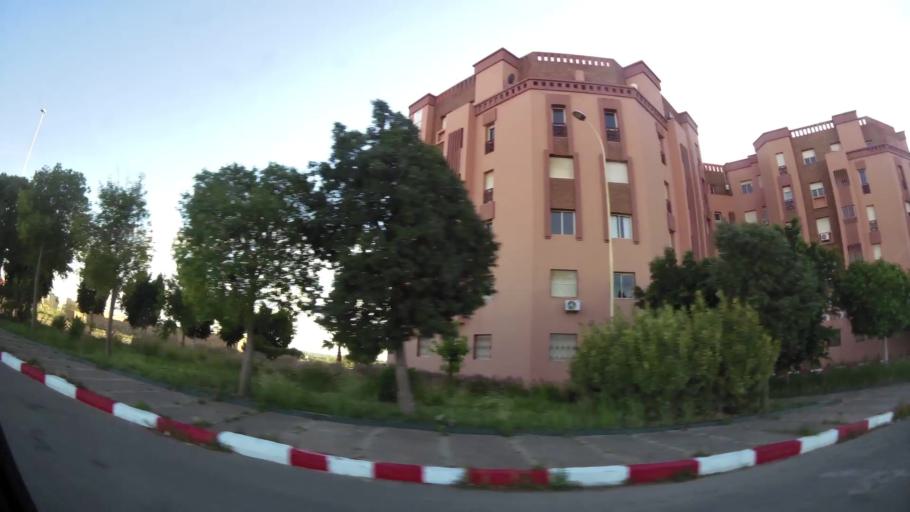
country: MA
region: Marrakech-Tensift-Al Haouz
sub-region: Marrakech
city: Marrakesh
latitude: 31.7462
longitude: -8.1279
